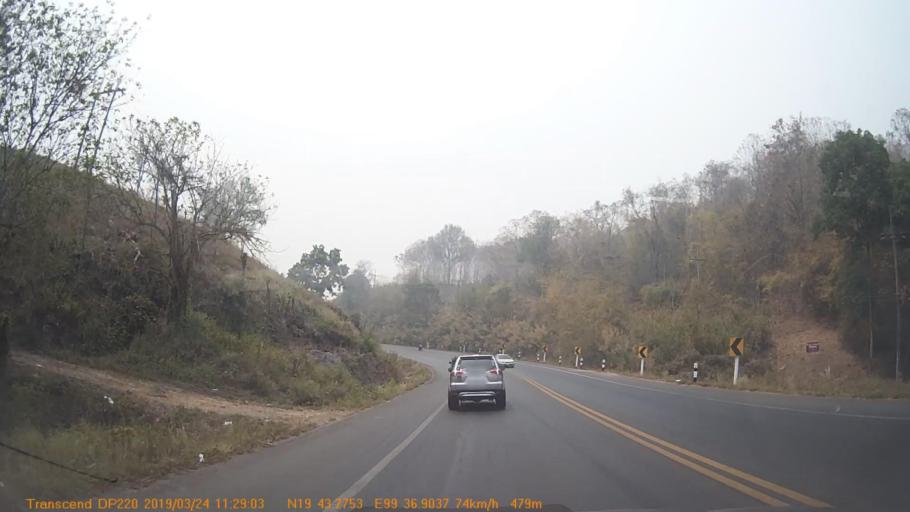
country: TH
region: Chiang Rai
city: Mae Lao
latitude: 19.7310
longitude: 99.6153
